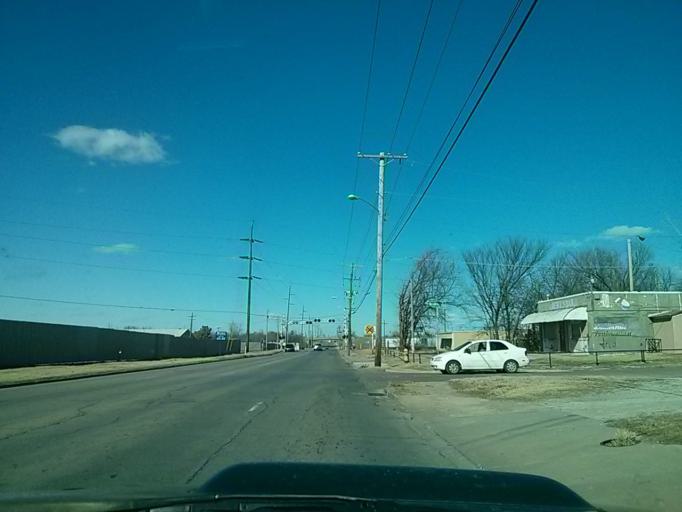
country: US
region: Oklahoma
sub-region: Tulsa County
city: Tulsa
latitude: 36.1854
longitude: -95.9582
